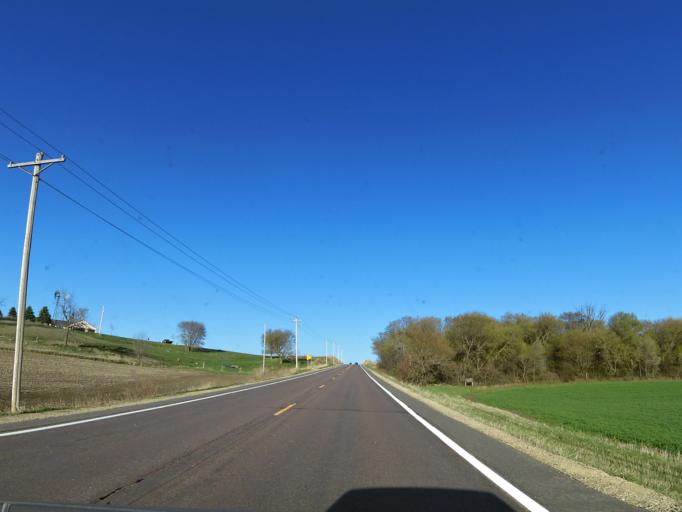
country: US
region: Minnesota
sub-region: Goodhue County
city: Cannon Falls
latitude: 44.6012
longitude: -92.8966
